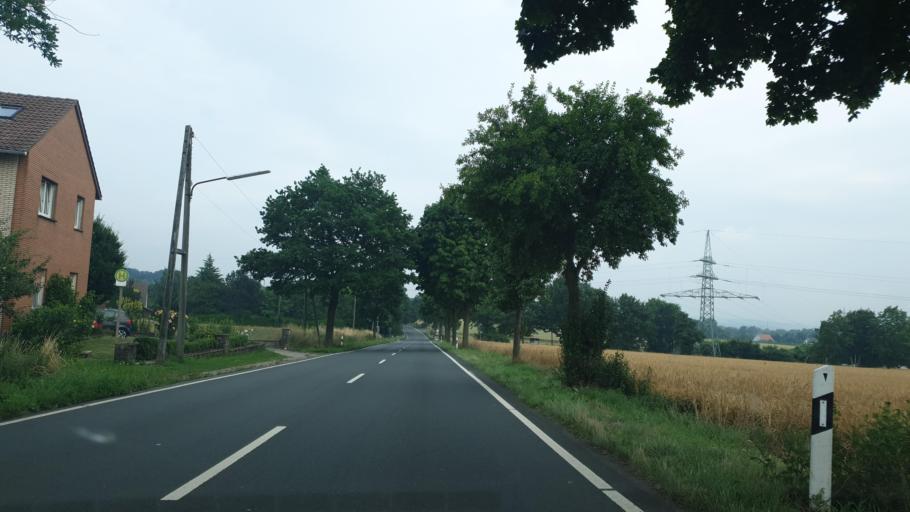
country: DE
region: North Rhine-Westphalia
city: Bad Oeynhausen
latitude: 52.2496
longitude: 8.7965
